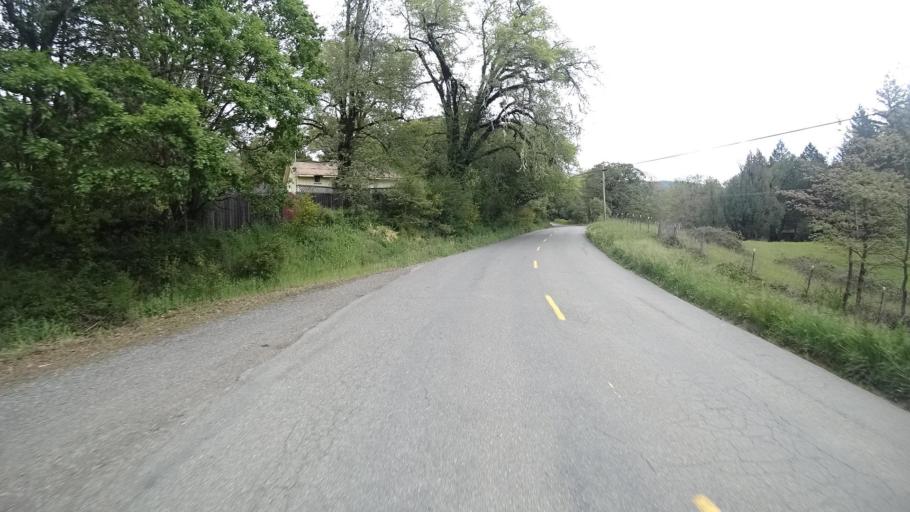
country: US
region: California
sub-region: Humboldt County
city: Redway
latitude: 40.1043
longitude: -123.9061
